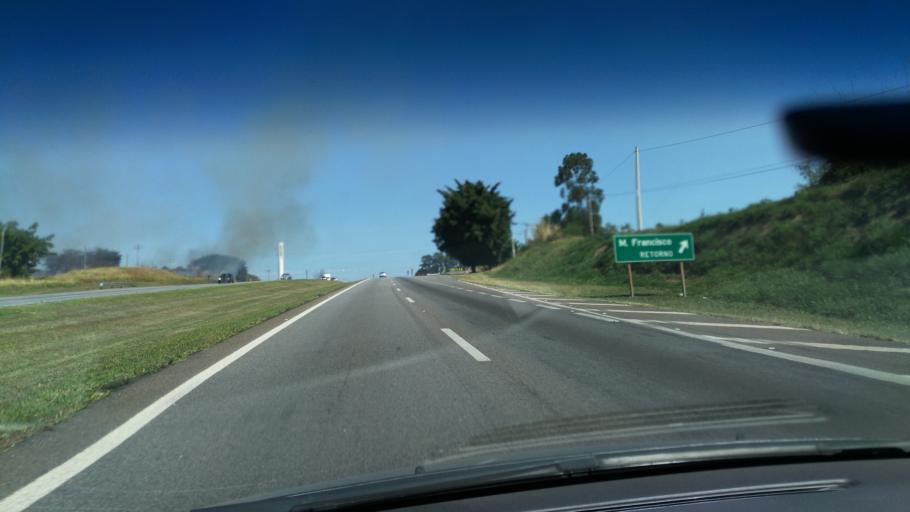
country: BR
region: Sao Paulo
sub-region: Mogi-Mirim
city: Mogi Mirim
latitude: -22.5024
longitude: -46.9854
